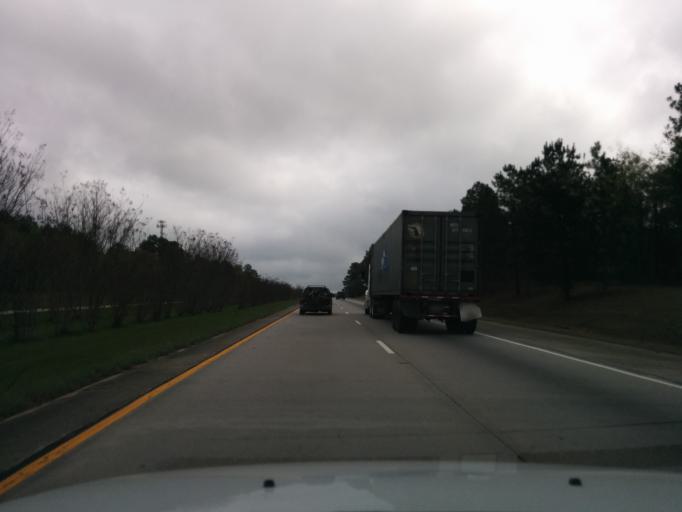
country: US
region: Georgia
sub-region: Candler County
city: Metter
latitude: 32.3815
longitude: -82.2197
